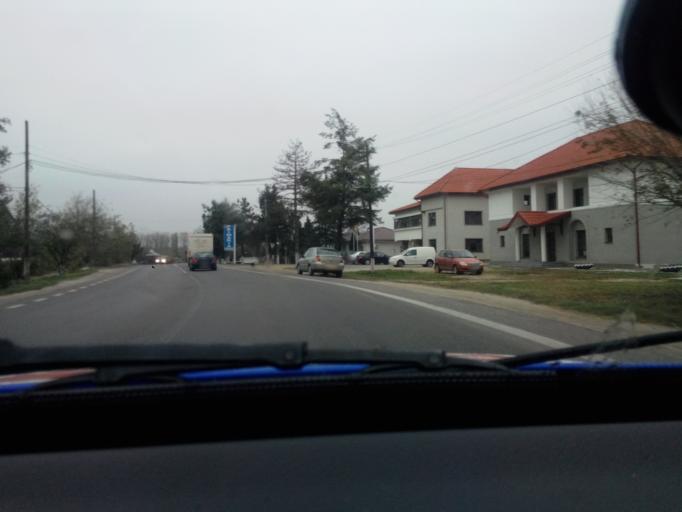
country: RO
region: Giurgiu
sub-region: Comuna Ghimpati
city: Ghimpati
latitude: 44.1905
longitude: 25.7764
